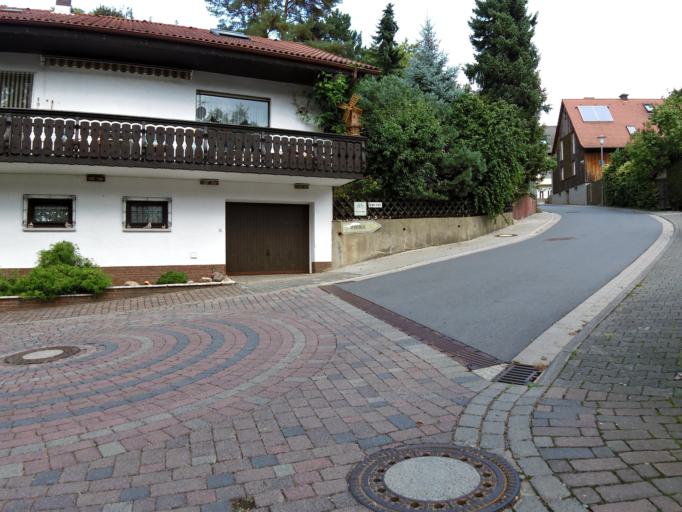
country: DE
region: Hesse
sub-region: Regierungsbezirk Darmstadt
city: Brensbach
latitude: 49.7622
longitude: 8.9103
